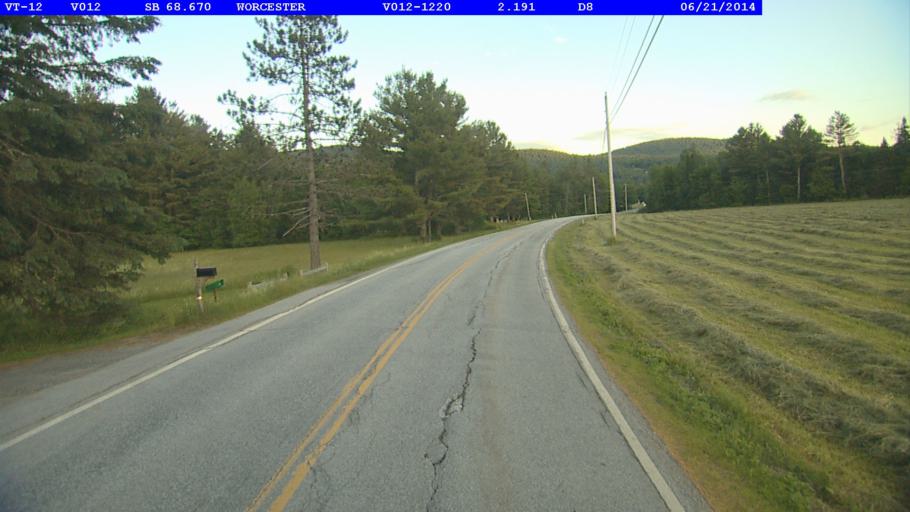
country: US
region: Vermont
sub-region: Washington County
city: Montpelier
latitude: 44.3803
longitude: -72.5501
